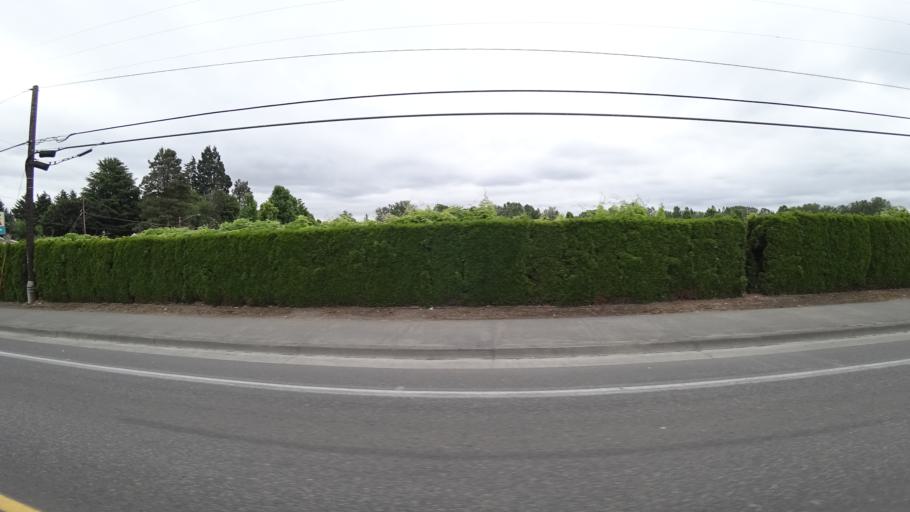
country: US
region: Washington
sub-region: Clark County
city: Vancouver
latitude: 45.6006
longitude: -122.6528
